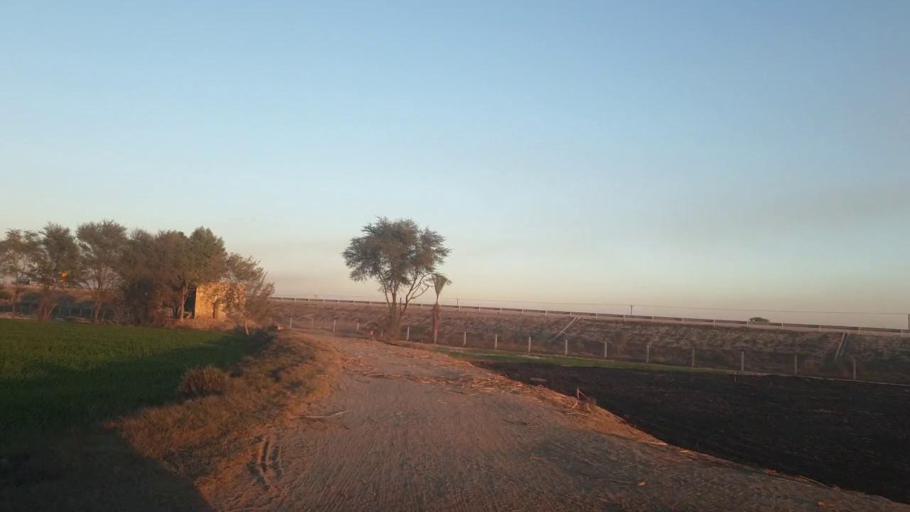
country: PK
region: Sindh
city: Ghotki
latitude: 28.0330
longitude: 69.3089
